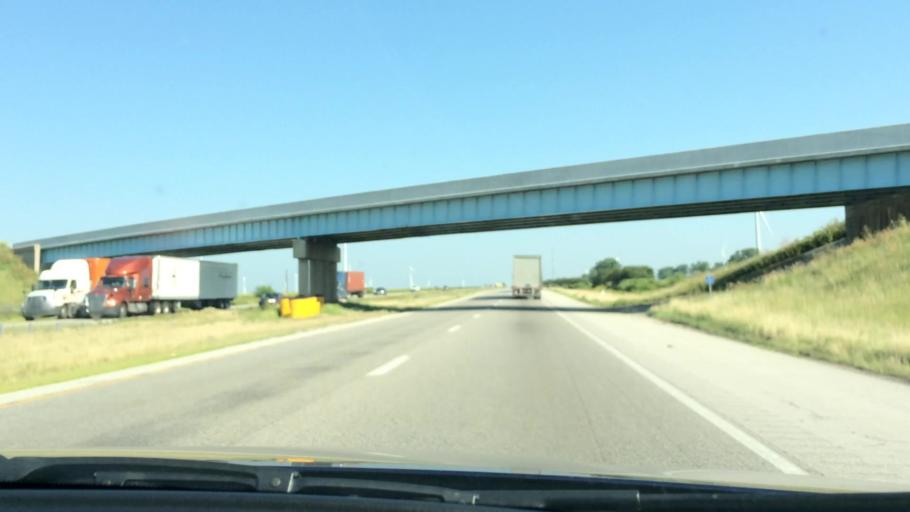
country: US
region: Indiana
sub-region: White County
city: Wolcott
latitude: 40.6351
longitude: -87.0056
